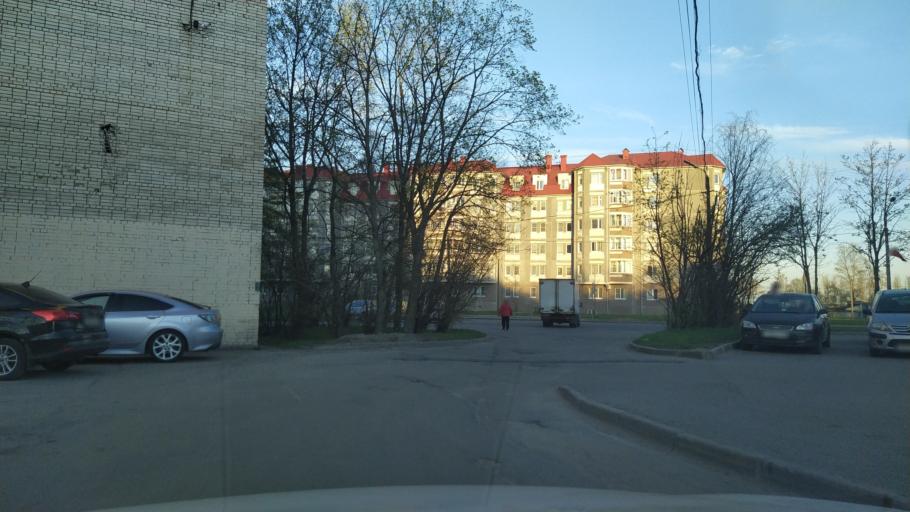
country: RU
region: St.-Petersburg
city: Pushkin
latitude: 59.7043
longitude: 30.3717
